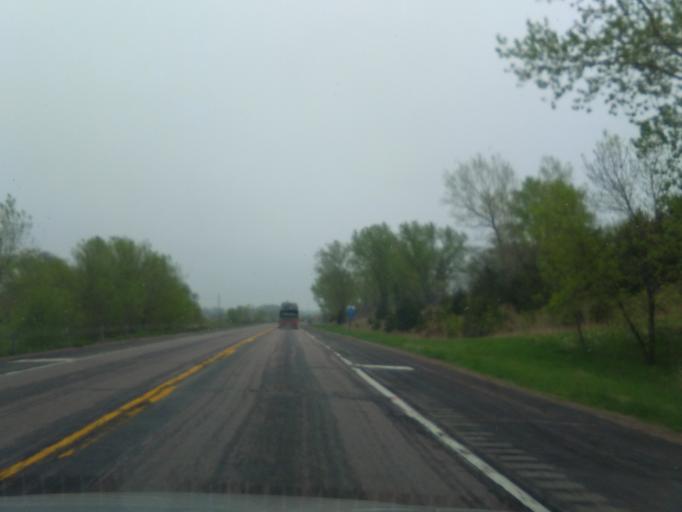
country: US
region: Nebraska
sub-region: Burt County
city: Oakland
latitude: 41.7989
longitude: -96.4826
